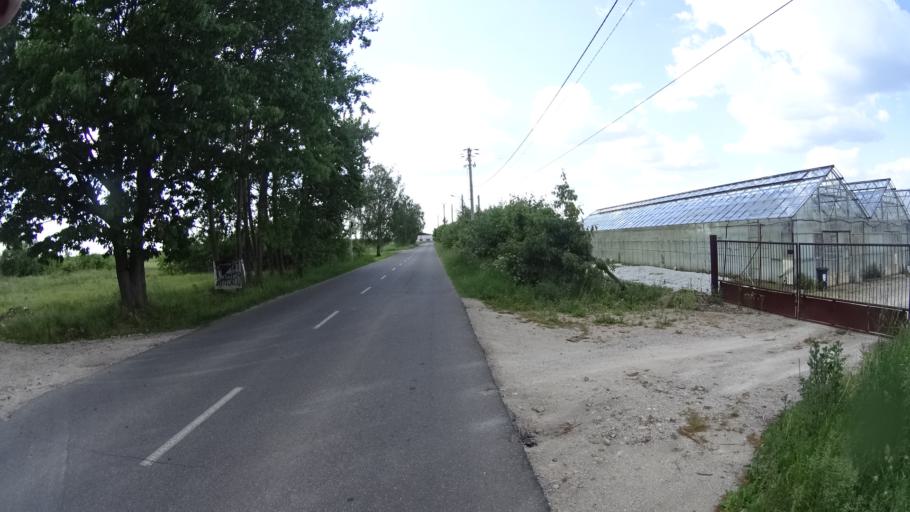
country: PL
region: Masovian Voivodeship
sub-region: Powiat piaseczynski
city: Tarczyn
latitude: 52.0109
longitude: 20.8213
